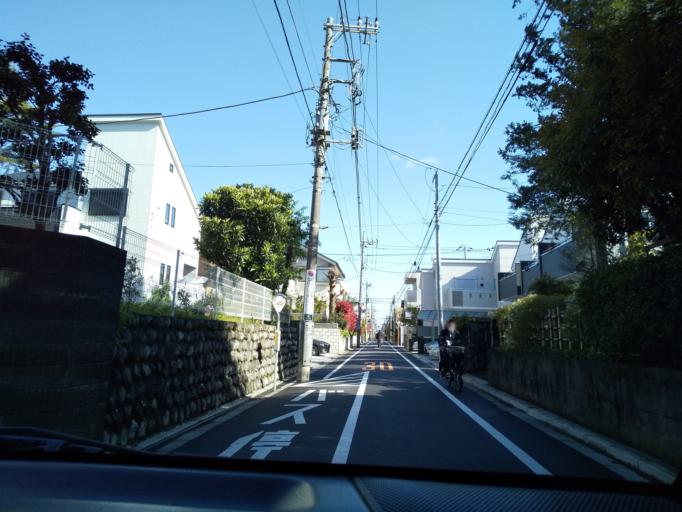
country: JP
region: Tokyo
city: Kokubunji
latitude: 35.6912
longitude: 139.4388
